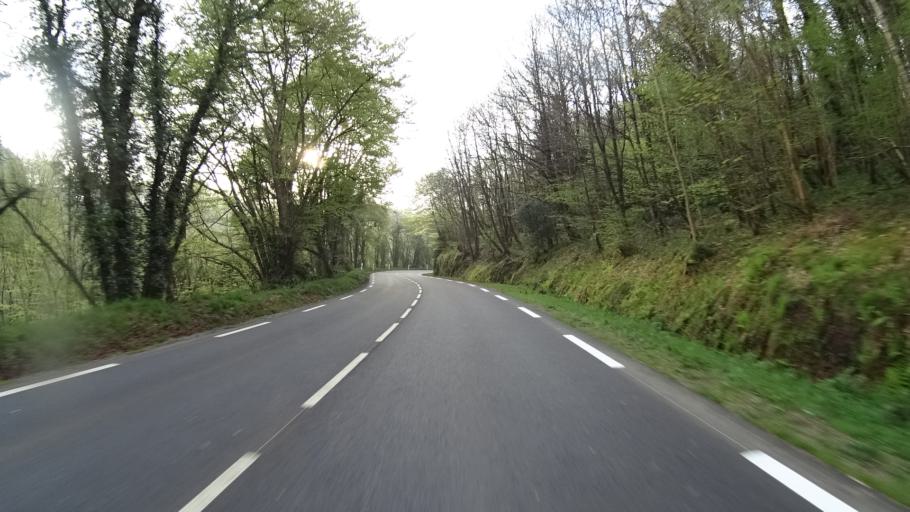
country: FR
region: Brittany
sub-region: Departement du Finistere
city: La Roche-Maurice
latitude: 48.4646
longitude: -4.1992
